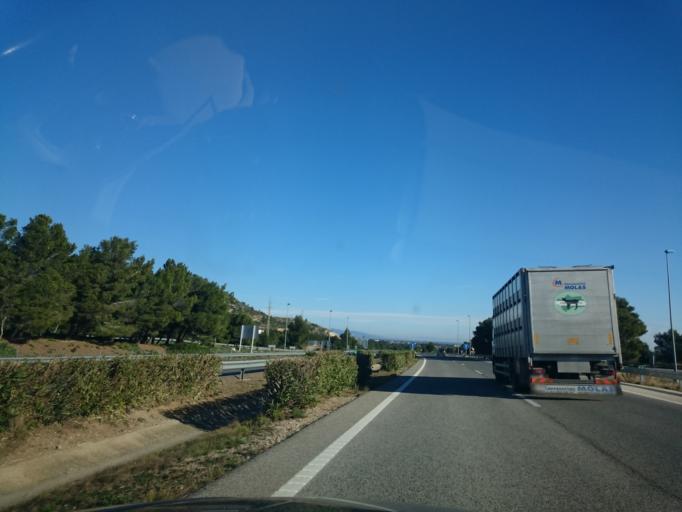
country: ES
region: Catalonia
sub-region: Provincia de Tarragona
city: Colldejou
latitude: 40.9861
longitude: 0.8966
